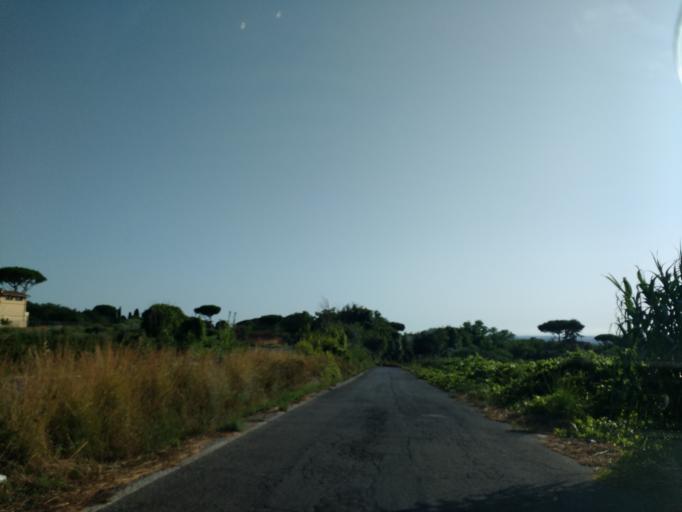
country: IT
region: Latium
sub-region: Citta metropolitana di Roma Capitale
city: Marino
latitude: 41.7549
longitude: 12.6378
